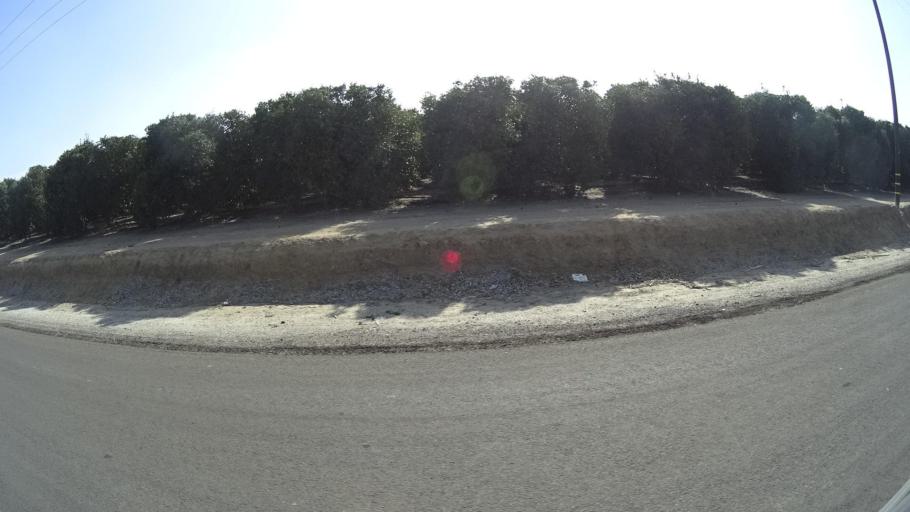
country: US
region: California
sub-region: Kern County
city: McFarland
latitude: 35.6311
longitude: -119.1742
